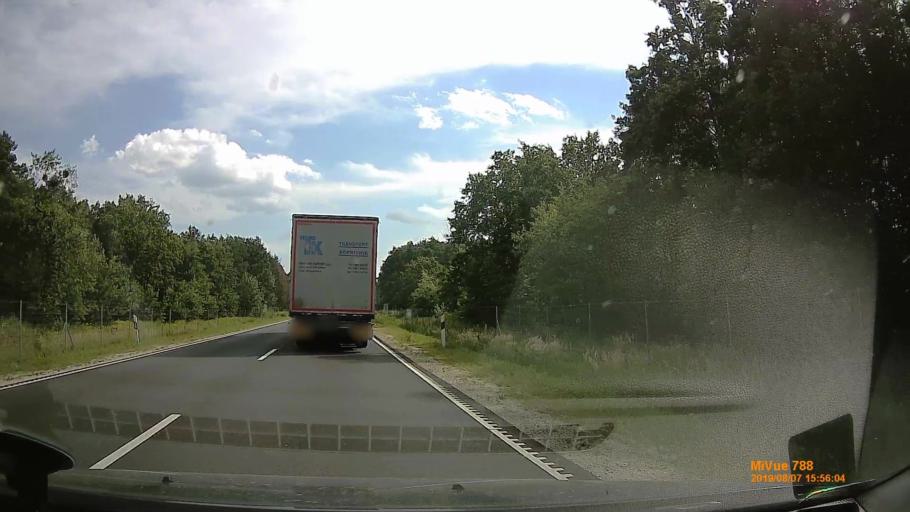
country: HU
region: Vas
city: Kormend
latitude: 47.0658
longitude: 16.6167
